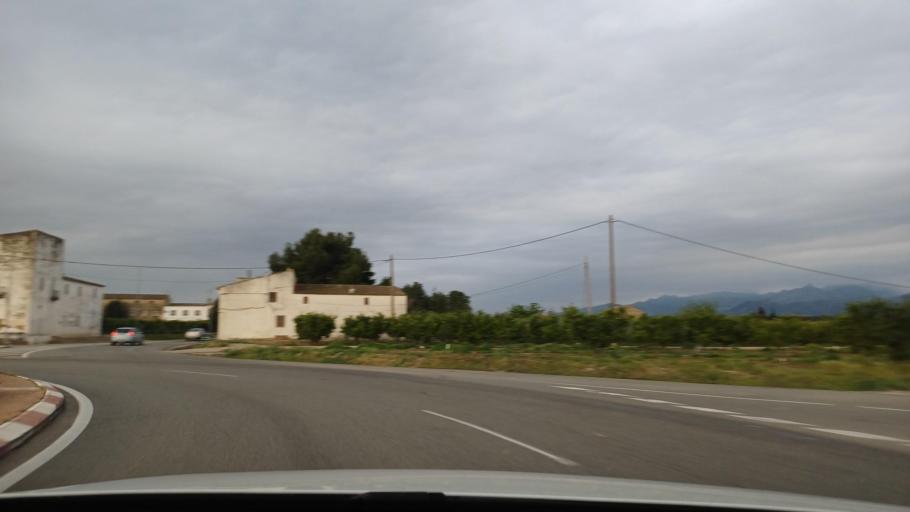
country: ES
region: Catalonia
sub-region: Provincia de Tarragona
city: Tortosa
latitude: 40.8059
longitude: 0.5057
